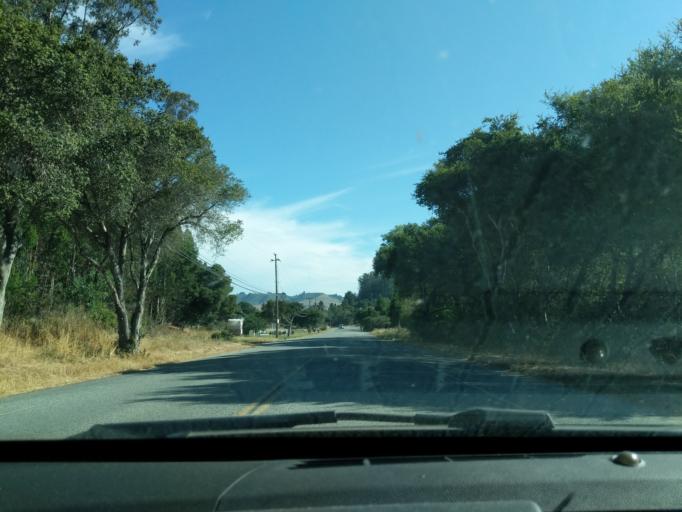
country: US
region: California
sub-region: San Benito County
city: Aromas
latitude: 36.8757
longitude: -121.6421
